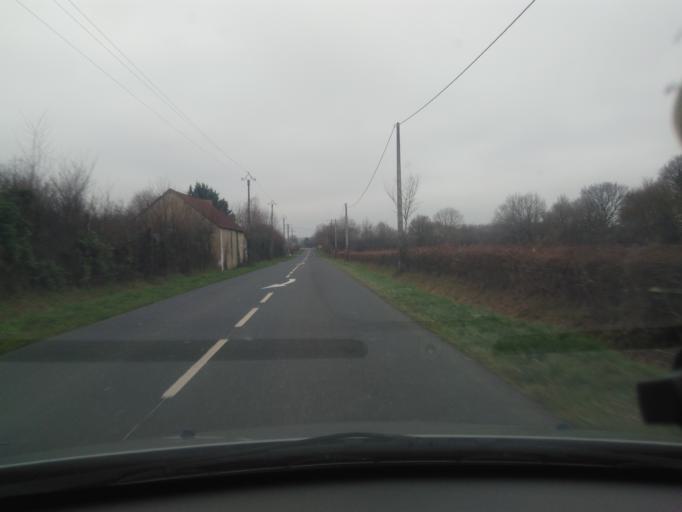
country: FR
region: Centre
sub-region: Departement de l'Indre
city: Montgivray
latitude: 46.6389
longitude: 2.0822
